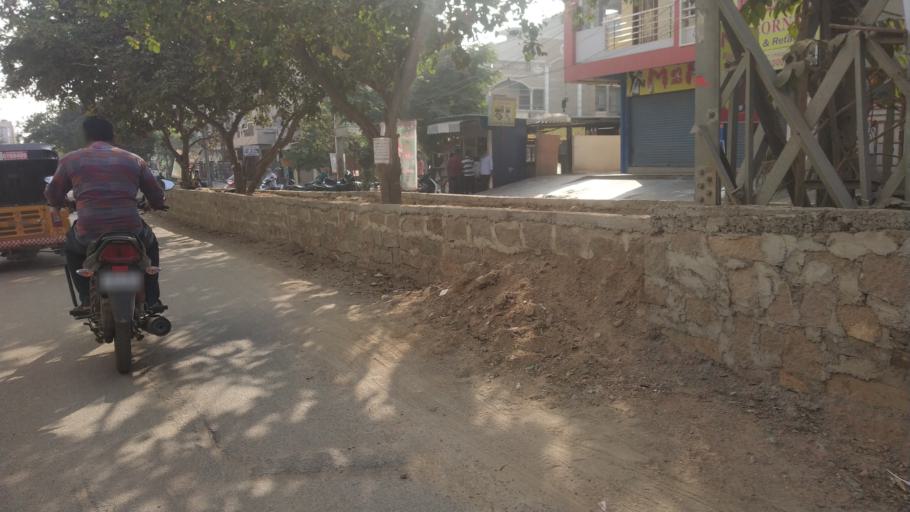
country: IN
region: Telangana
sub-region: Rangareddi
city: Kukatpalli
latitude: 17.5052
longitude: 78.3966
